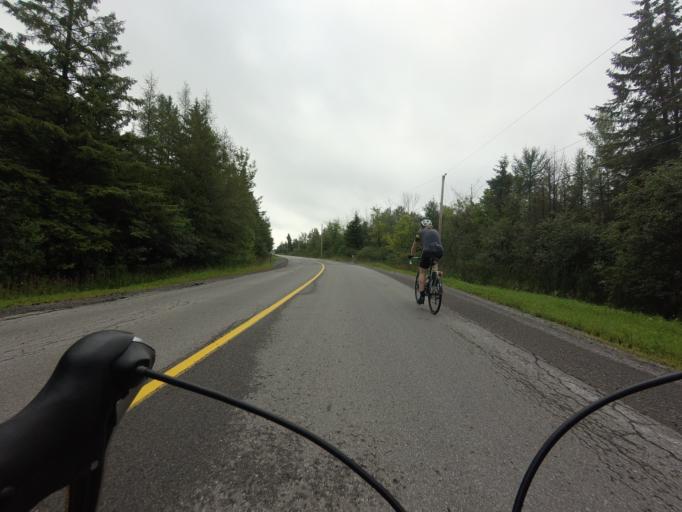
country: CA
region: Ontario
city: Bells Corners
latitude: 45.0794
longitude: -75.7433
